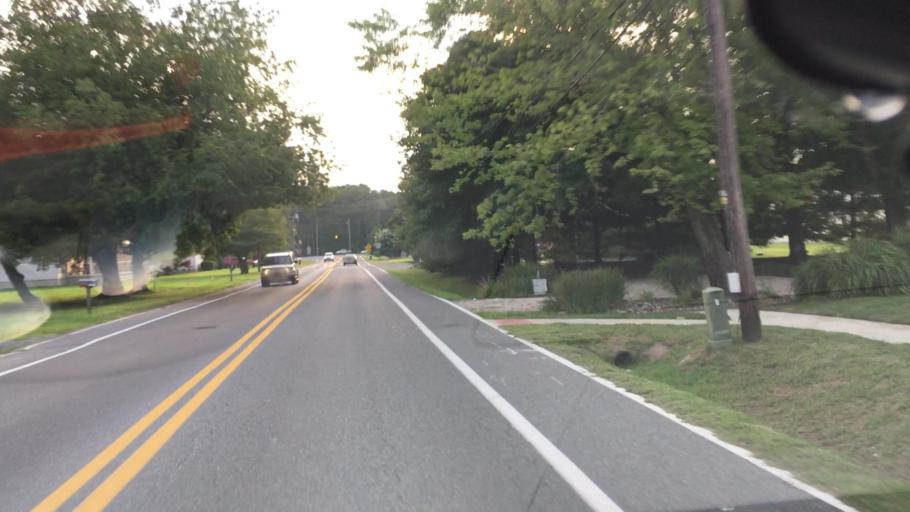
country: US
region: Delaware
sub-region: Sussex County
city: Ocean View
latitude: 38.5425
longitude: -75.0978
